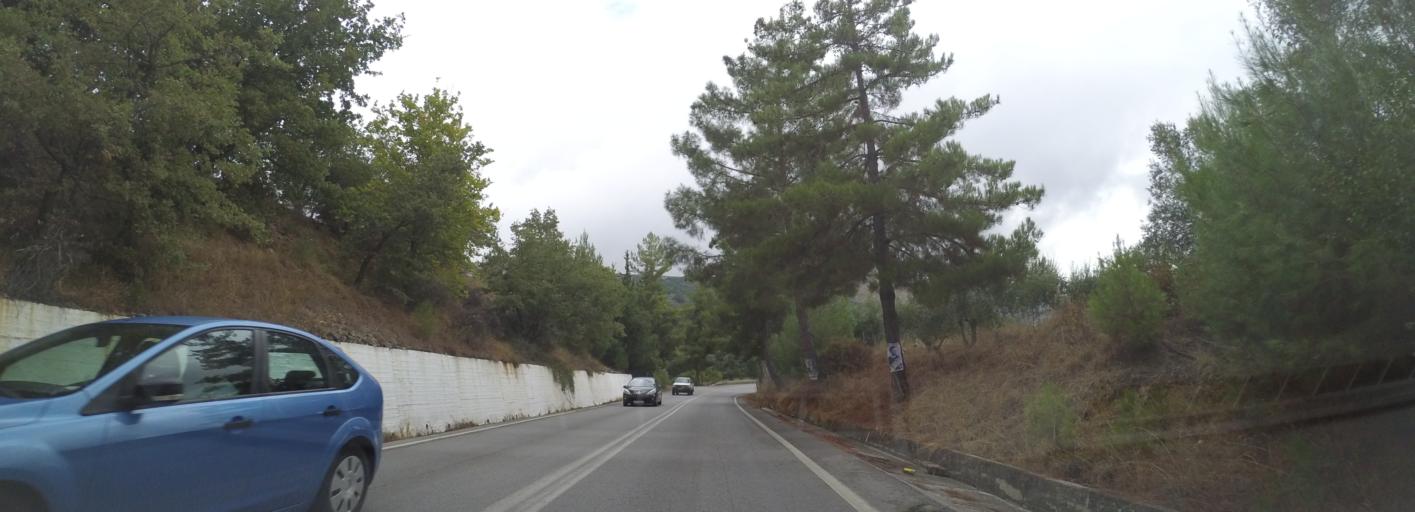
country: GR
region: Crete
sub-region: Nomos Rethymnis
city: Agia Foteini
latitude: 35.2205
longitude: 24.5256
